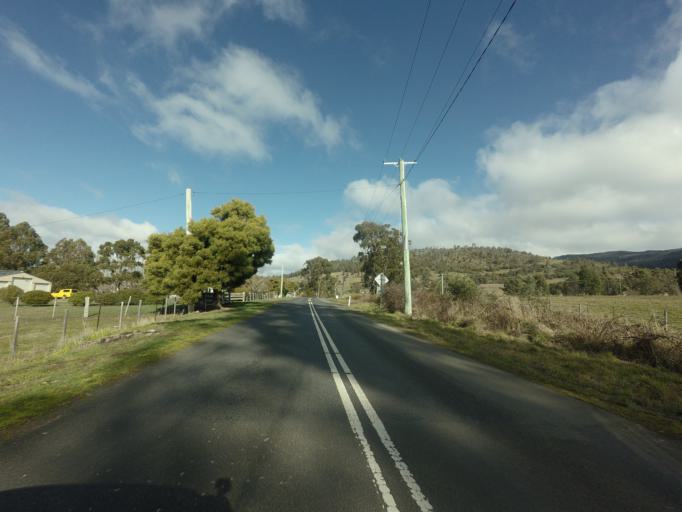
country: AU
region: Tasmania
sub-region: Derwent Valley
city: New Norfolk
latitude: -42.6035
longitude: 146.7062
